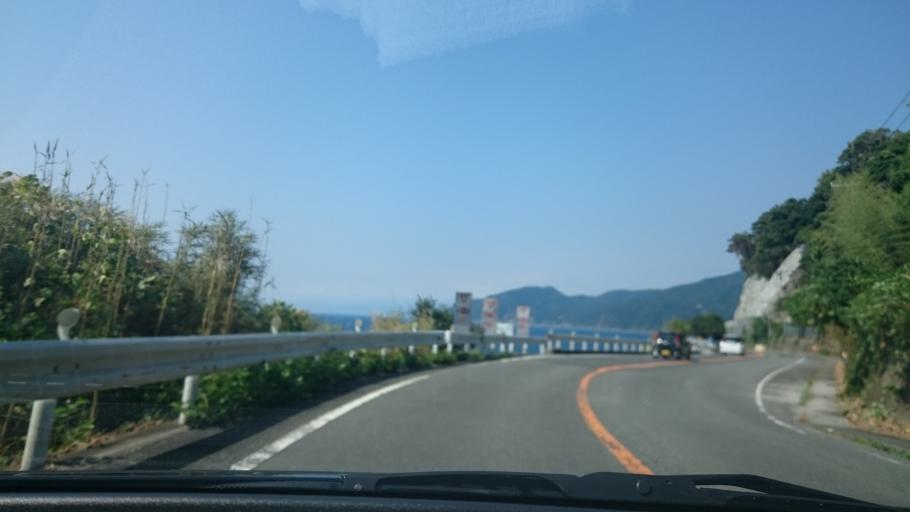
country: JP
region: Shizuoka
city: Heda
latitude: 34.8919
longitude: 138.7646
